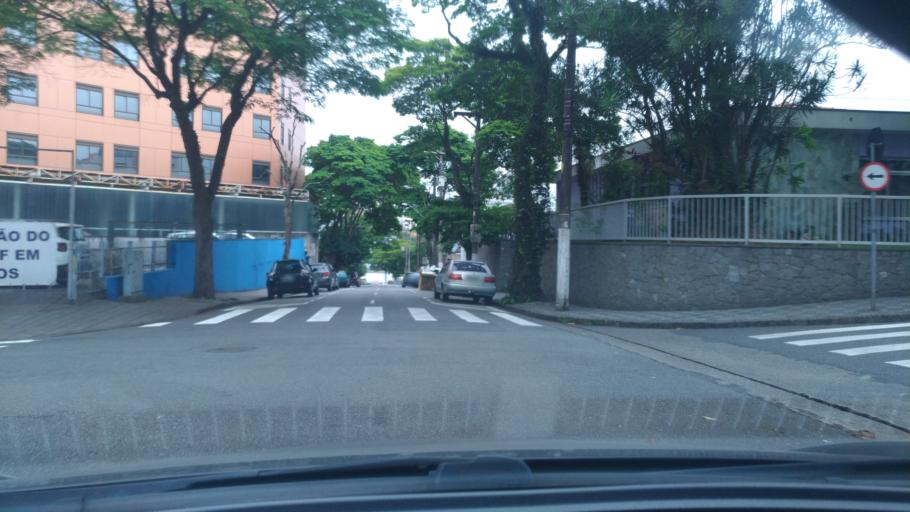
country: BR
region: Sao Paulo
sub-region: Sao Bernardo Do Campo
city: Sao Bernardo do Campo
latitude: -23.7032
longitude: -46.5490
